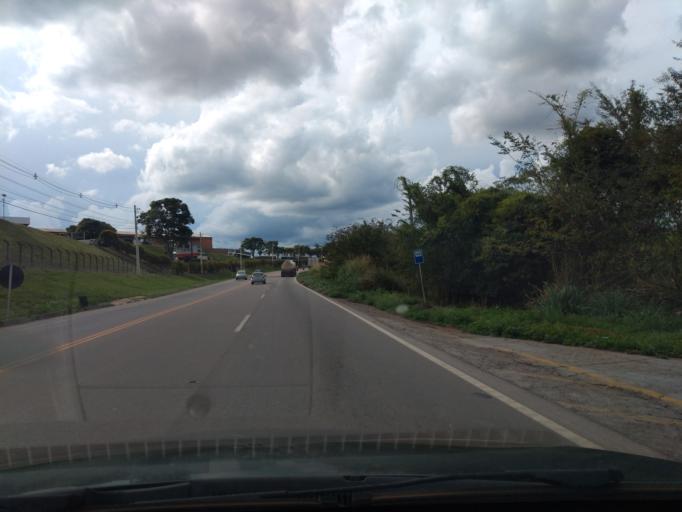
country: BR
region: Minas Gerais
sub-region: Varginha
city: Varginha
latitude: -21.6012
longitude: -45.4371
